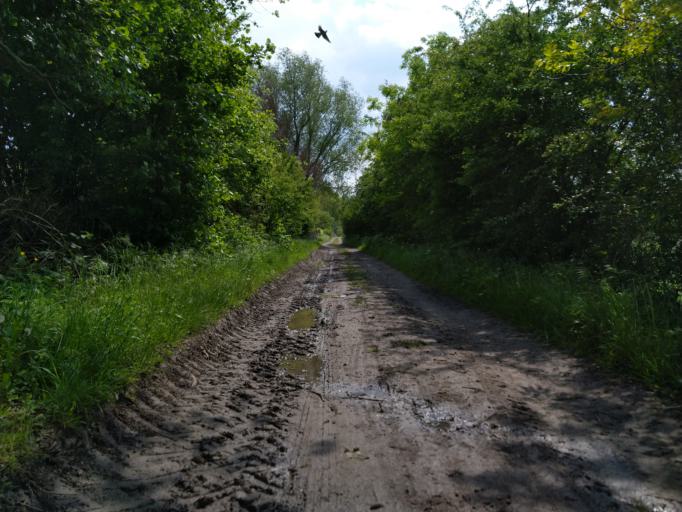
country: BE
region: Wallonia
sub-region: Province du Hainaut
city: Mons
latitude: 50.4448
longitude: 3.9834
